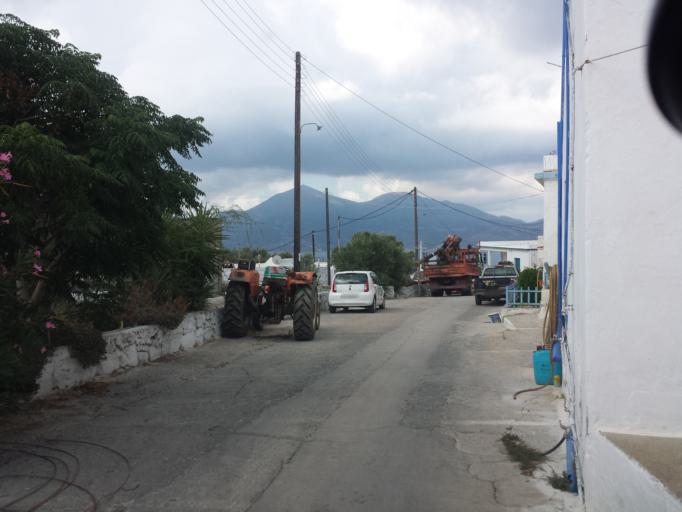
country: GR
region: South Aegean
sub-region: Nomos Kykladon
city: Milos
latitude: 36.7406
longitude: 24.4248
